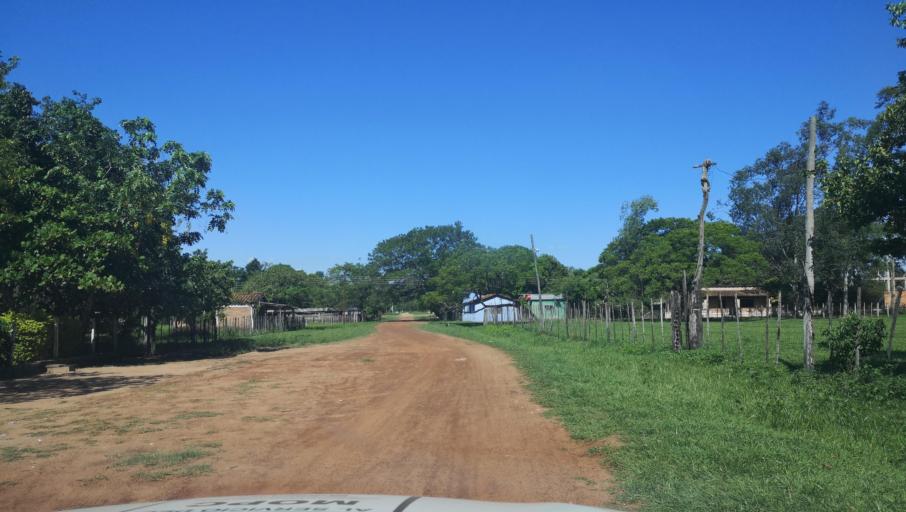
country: PY
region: Caaguazu
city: Carayao
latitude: -25.1937
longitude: -56.4013
